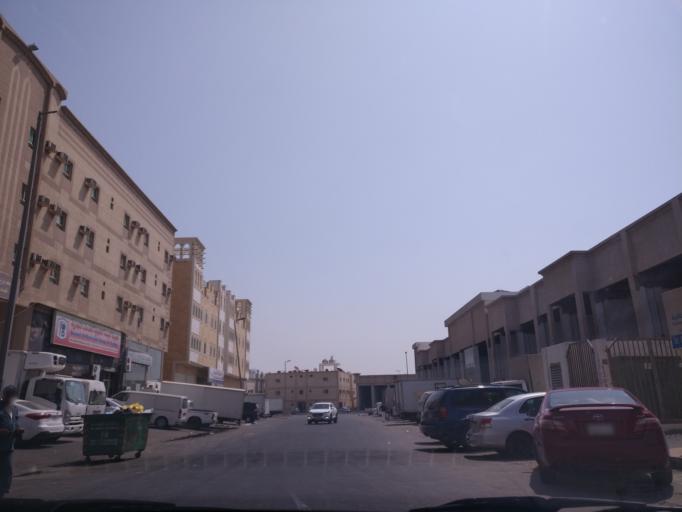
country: SA
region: Eastern Province
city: Dammam
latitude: 26.4445
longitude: 50.0683
